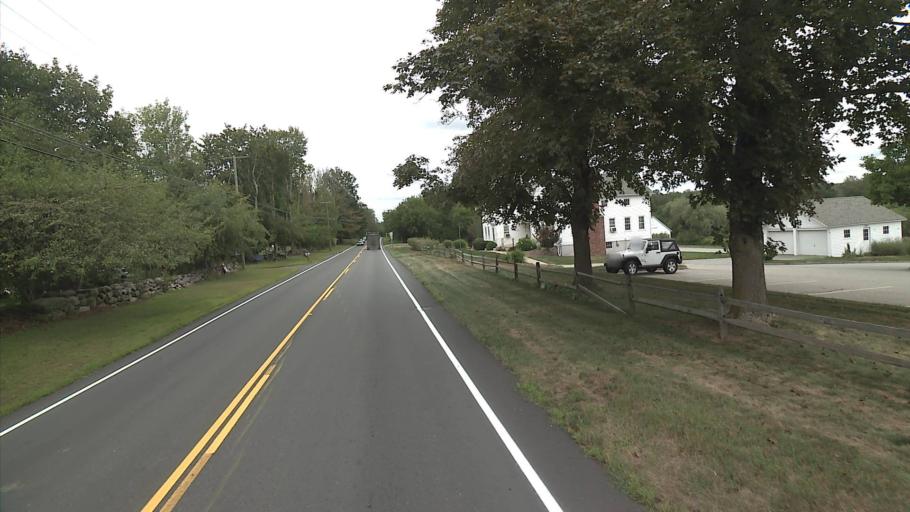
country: US
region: Connecticut
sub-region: Tolland County
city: Hebron
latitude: 41.6467
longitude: -72.3584
